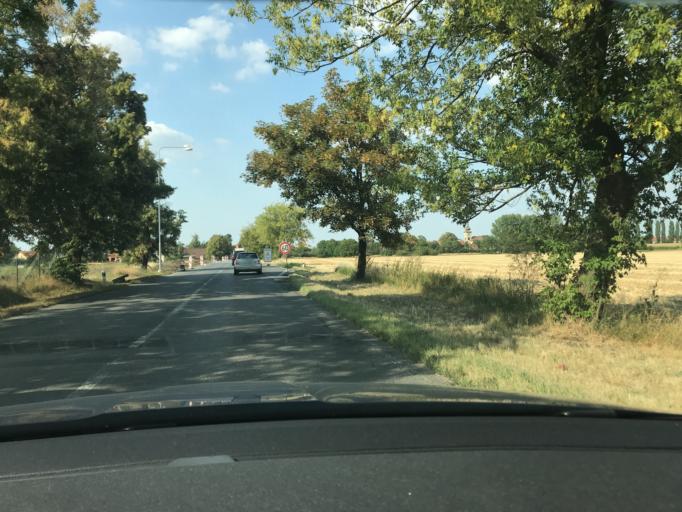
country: CZ
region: Central Bohemia
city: Velke Prilepy
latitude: 50.1850
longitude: 14.3209
